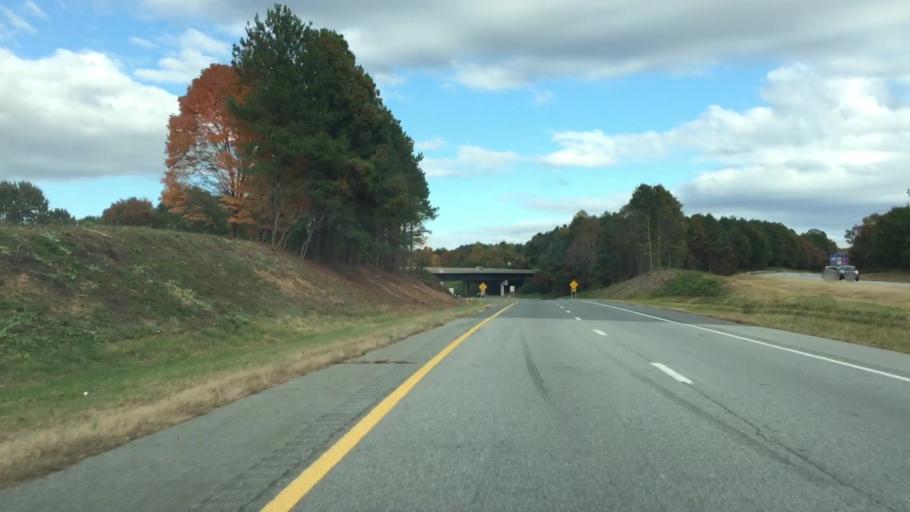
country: US
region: North Carolina
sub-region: Forsyth County
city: Clemmons
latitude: 36.0703
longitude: -80.3284
